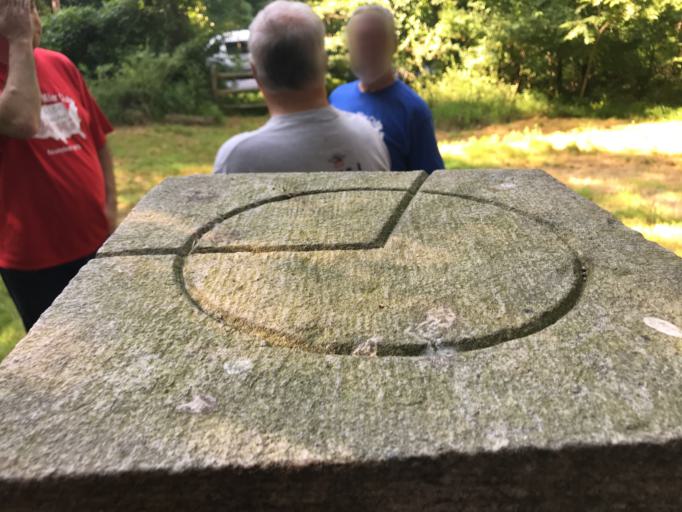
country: US
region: Delaware
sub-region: New Castle County
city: Newark
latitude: 39.7222
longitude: -75.7738
